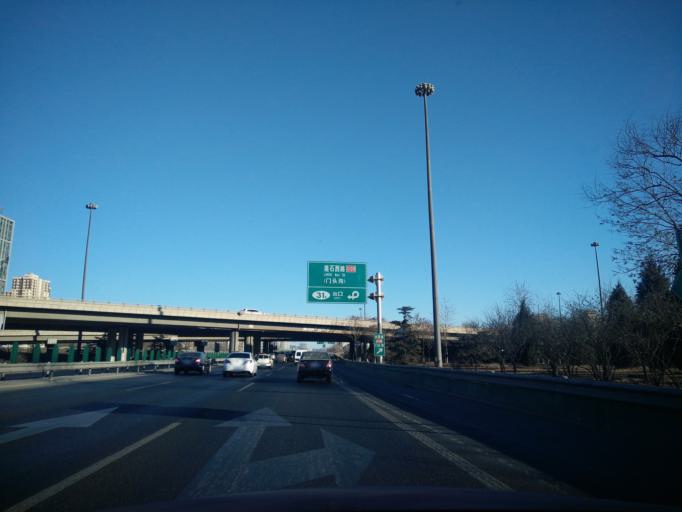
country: CN
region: Beijing
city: Lugu
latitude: 39.8920
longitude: 116.2053
